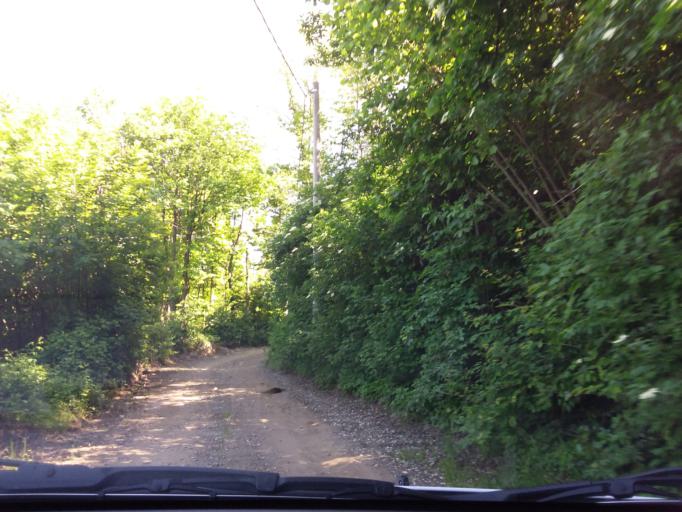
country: IT
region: Piedmont
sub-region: Provincia di Torino
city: Rosta
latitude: 45.0612
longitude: 7.4909
